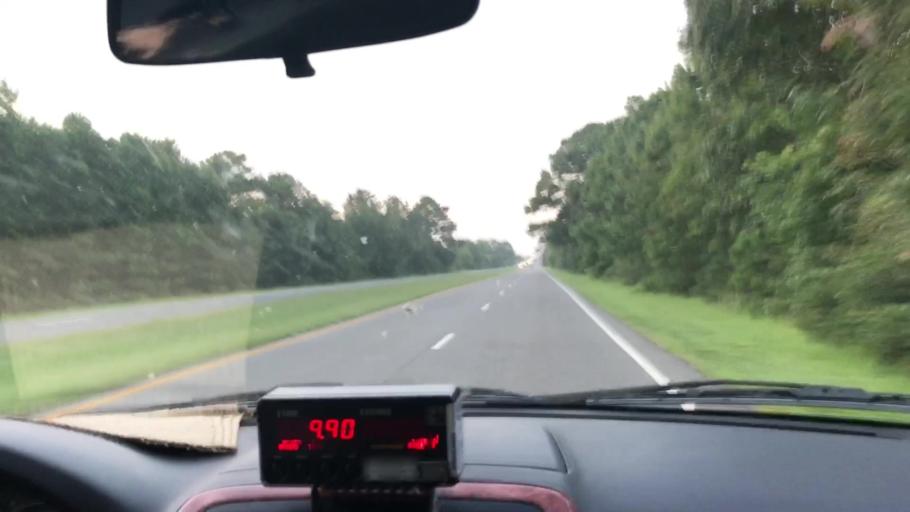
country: US
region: Virginia
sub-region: City of Hampton
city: Hampton
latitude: 37.0537
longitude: -76.3657
